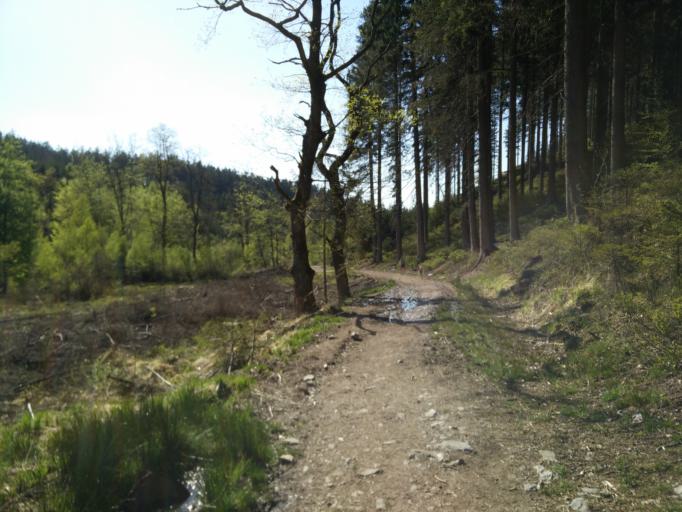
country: BE
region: Wallonia
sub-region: Province de Liege
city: Raeren
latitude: 50.5945
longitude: 6.1374
